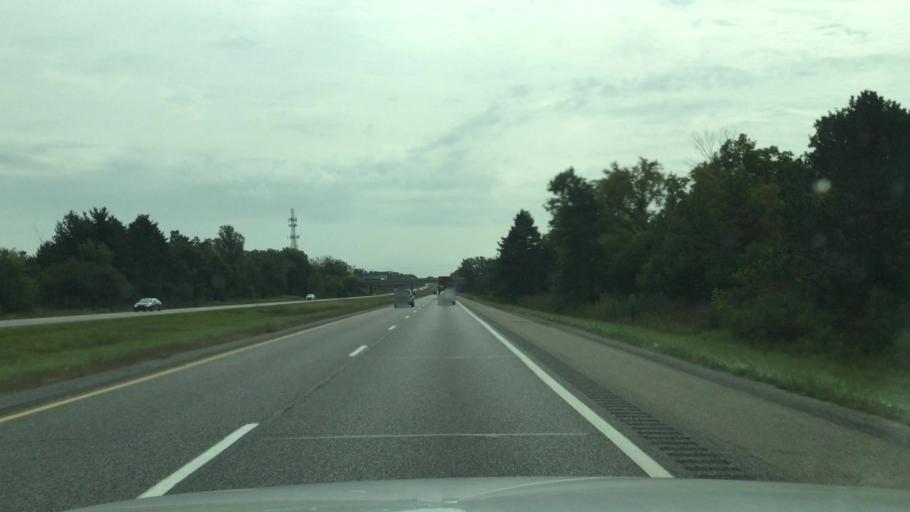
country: US
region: Michigan
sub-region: Genesee County
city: Flint
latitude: 42.9471
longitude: -83.7175
